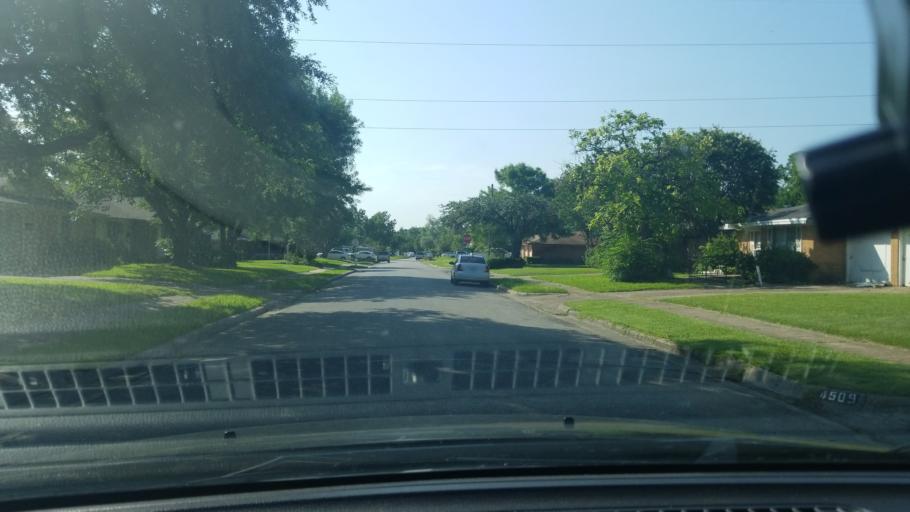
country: US
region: Texas
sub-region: Dallas County
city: Mesquite
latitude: 32.8257
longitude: -96.6412
